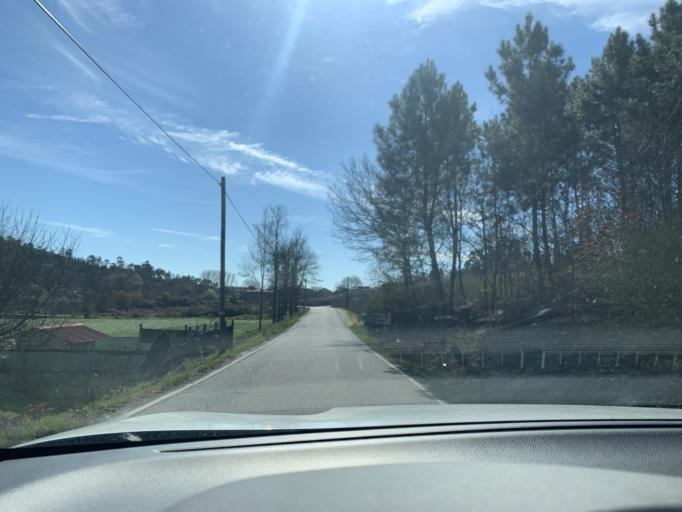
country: PT
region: Viseu
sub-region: Concelho de Tondela
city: Tondela
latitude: 40.5956
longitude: -8.0241
